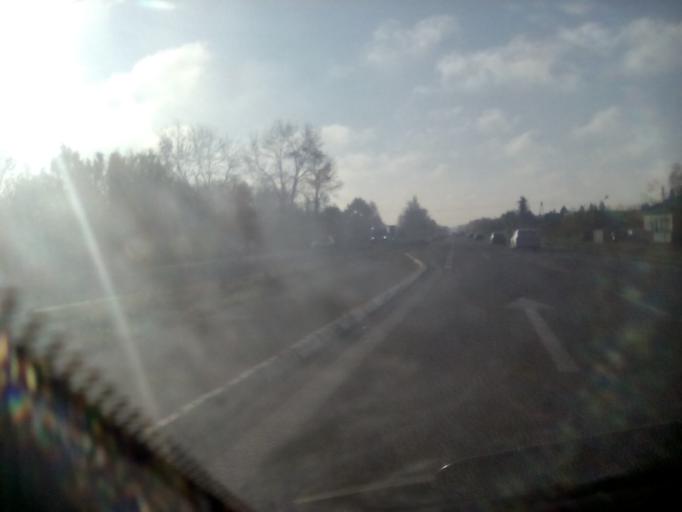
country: PL
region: Masovian Voivodeship
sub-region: Powiat piaseczynski
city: Tarczyn
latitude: 51.9330
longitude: 20.8483
